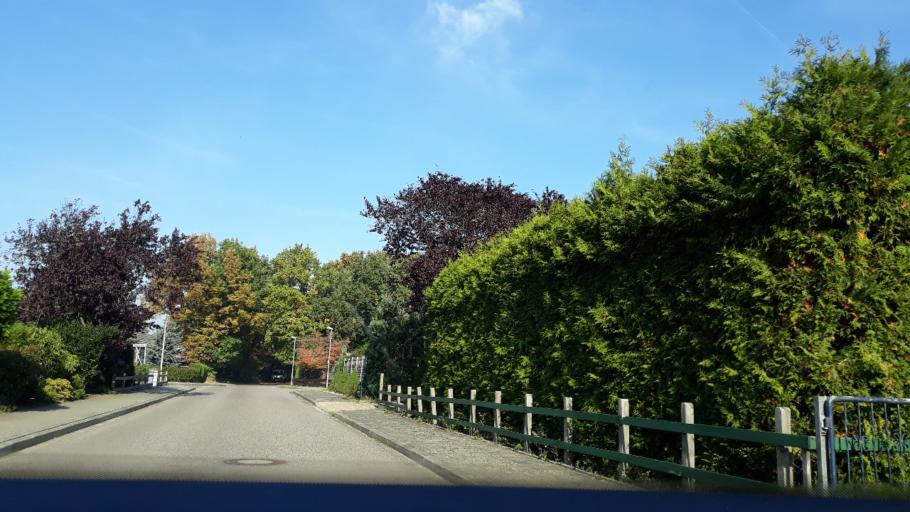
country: DE
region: Schleswig-Holstein
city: Kropp
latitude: 54.4126
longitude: 9.5178
